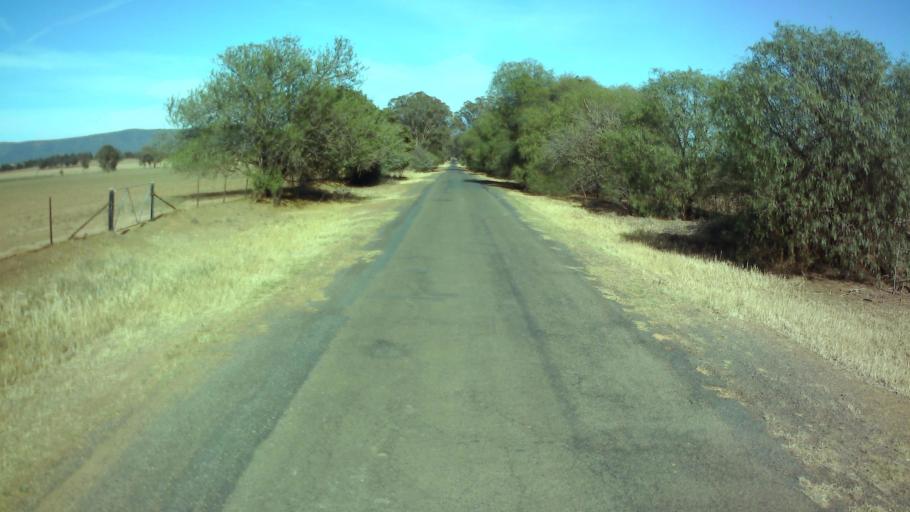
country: AU
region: New South Wales
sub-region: Weddin
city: Grenfell
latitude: -33.9075
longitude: 148.1051
